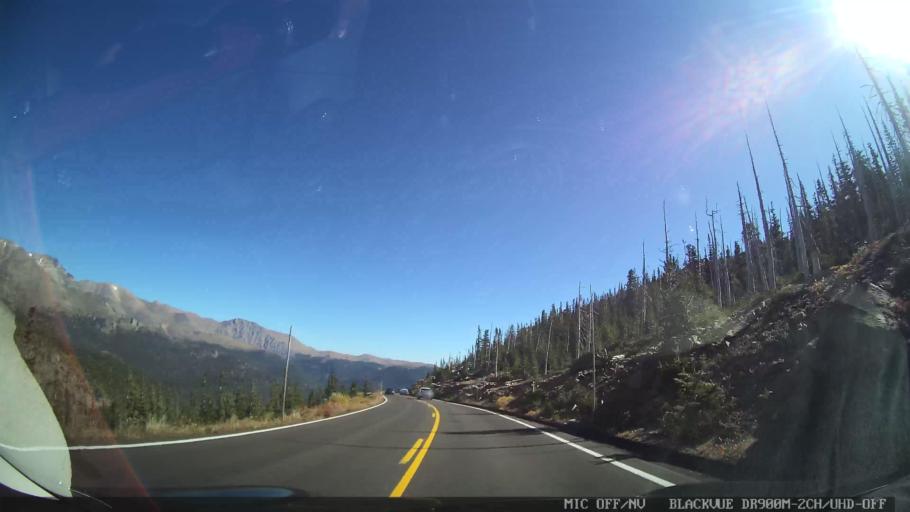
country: US
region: Colorado
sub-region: Larimer County
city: Estes Park
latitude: 40.3952
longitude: -105.6822
